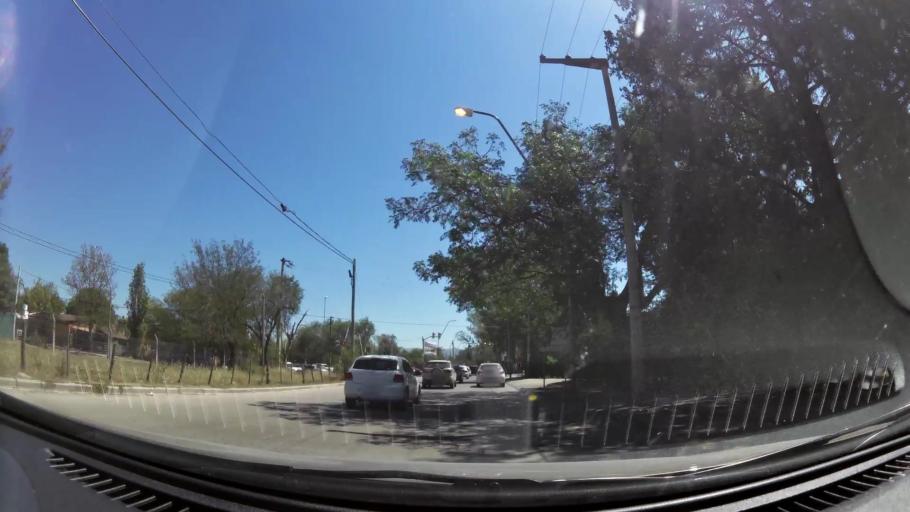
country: AR
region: Cordoba
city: Saldan
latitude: -31.3369
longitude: -64.2877
